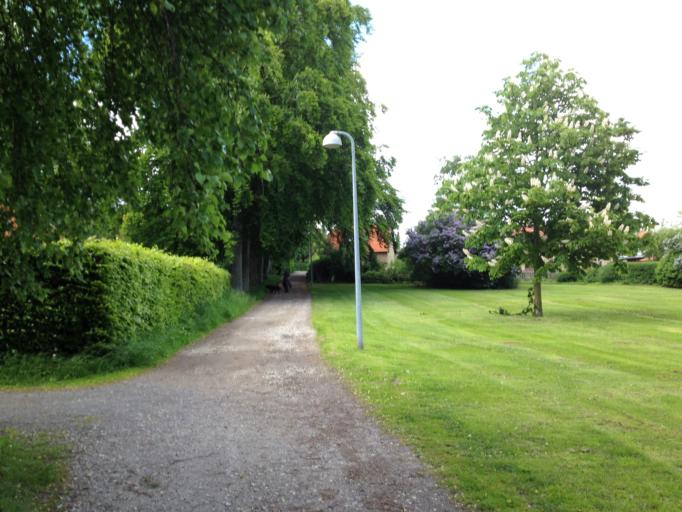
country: DK
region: Capital Region
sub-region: Fredensborg Kommune
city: Niva
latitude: 55.9298
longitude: 12.5088
